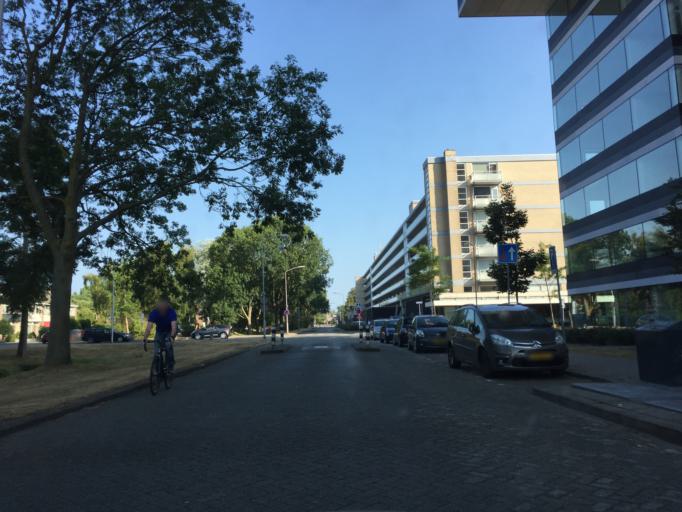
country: NL
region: South Holland
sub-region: Gemeente Wassenaar
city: Wassenaar
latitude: 52.0989
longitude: 4.4019
